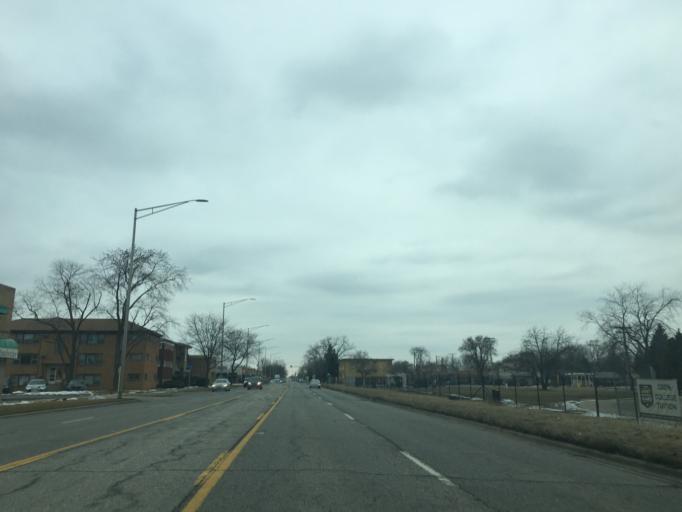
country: US
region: Illinois
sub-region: Cook County
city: North Riverside
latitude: 41.8498
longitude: -87.8406
